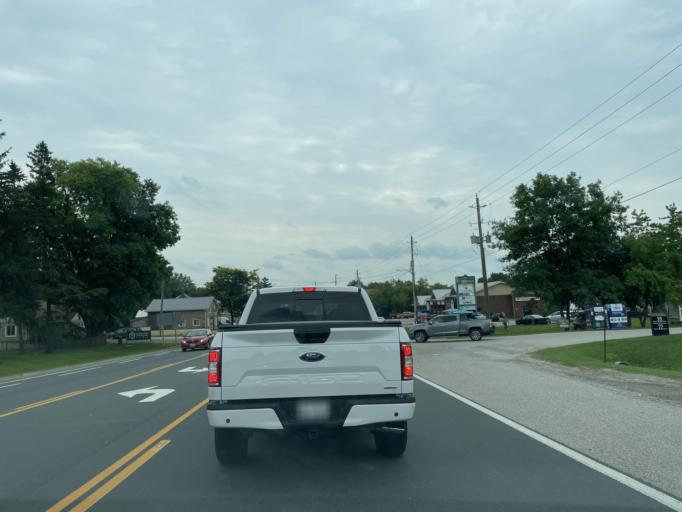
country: CA
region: Ontario
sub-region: Wellington County
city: Guelph
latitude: 43.4493
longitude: -80.1188
